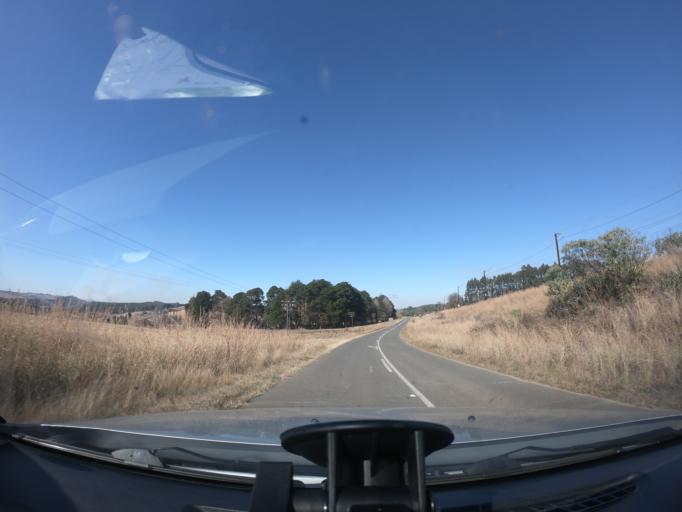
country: ZA
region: KwaZulu-Natal
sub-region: uMgungundlovu District Municipality
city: Howick
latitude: -29.4135
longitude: 30.0881
